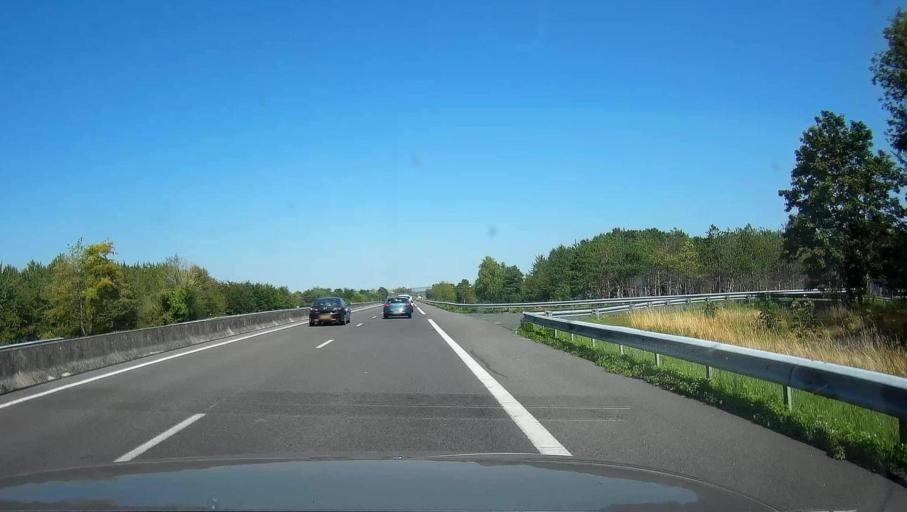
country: FR
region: Champagne-Ardenne
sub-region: Departement de l'Aube
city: Arcis-sur-Aube
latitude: 48.4923
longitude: 4.1651
